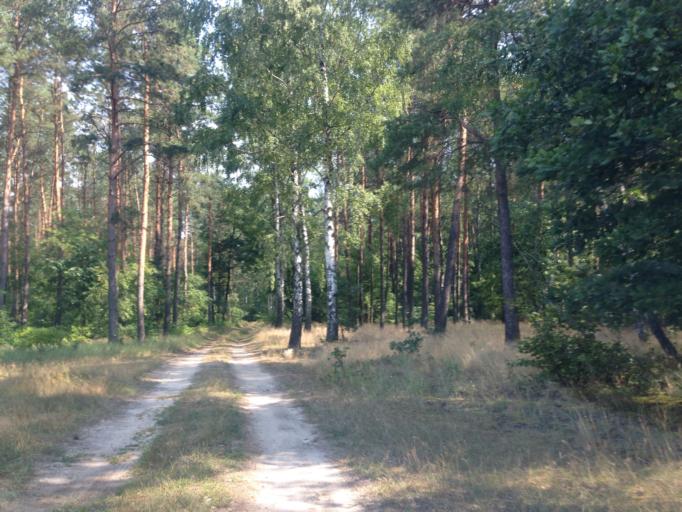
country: PL
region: Kujawsko-Pomorskie
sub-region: Powiat golubsko-dobrzynski
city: Golub-Dobrzyn
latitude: 53.1387
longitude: 19.0984
